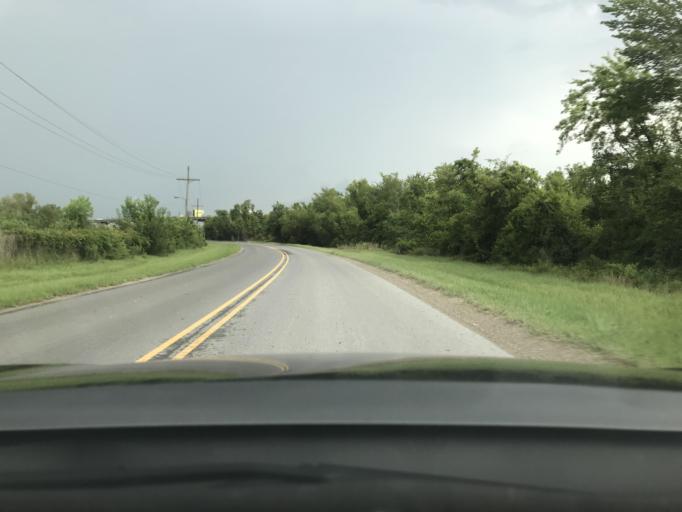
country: US
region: Louisiana
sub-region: Calcasieu Parish
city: Westlake
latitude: 30.2335
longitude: -93.2529
